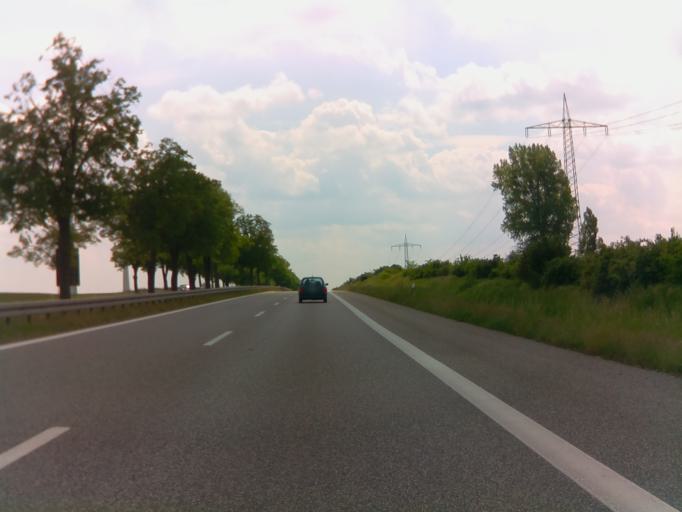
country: DE
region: Brandenburg
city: Wustermark
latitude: 52.5736
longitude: 12.9117
